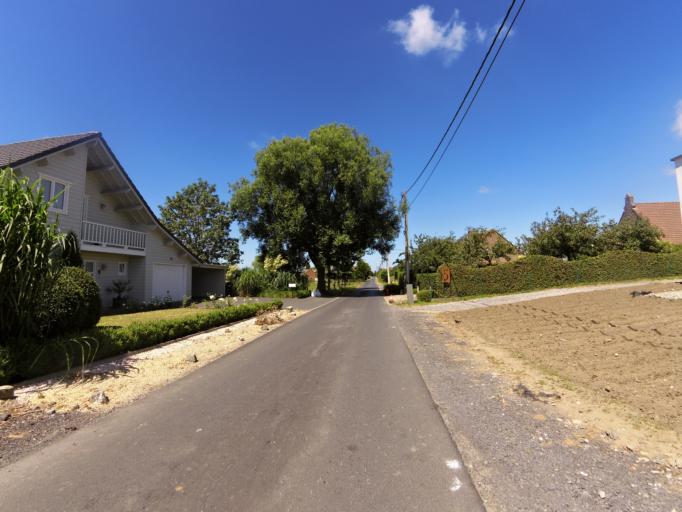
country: BE
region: Flanders
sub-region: Provincie West-Vlaanderen
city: Torhout
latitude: 51.0987
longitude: 3.0689
